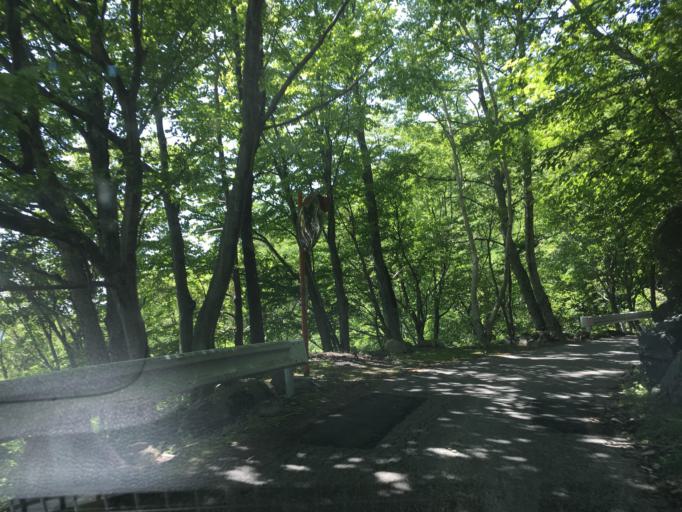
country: JP
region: Iwate
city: Ofunato
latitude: 39.1747
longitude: 141.7249
